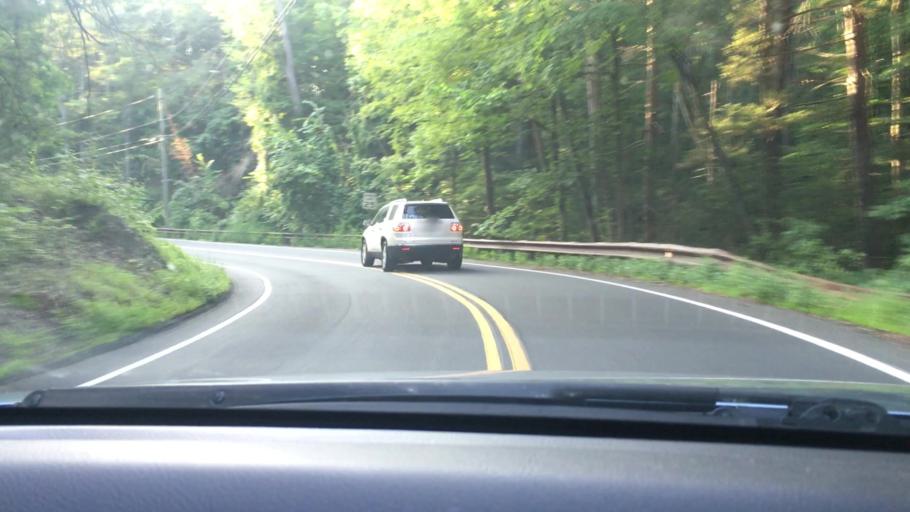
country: US
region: Connecticut
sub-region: Fairfield County
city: Georgetown
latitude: 41.2875
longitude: -73.3878
